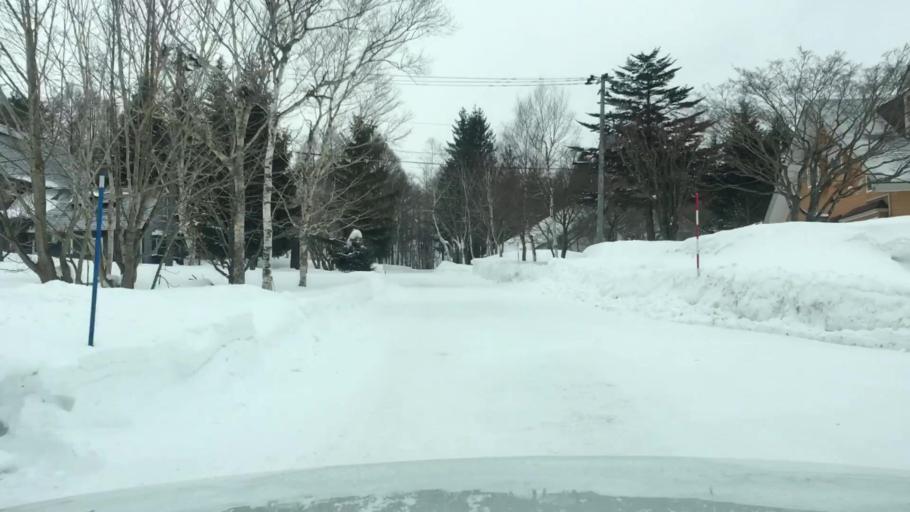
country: JP
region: Akita
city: Hanawa
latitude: 40.0050
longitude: 140.9773
